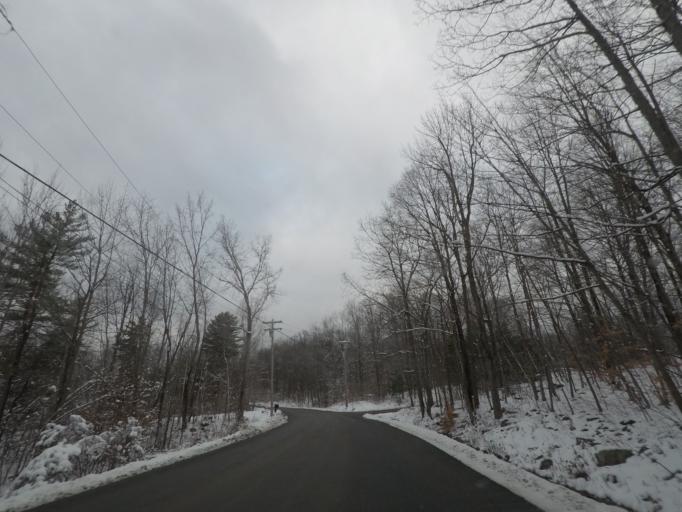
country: US
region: New York
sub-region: Rensselaer County
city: Averill Park
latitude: 42.6595
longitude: -73.5322
